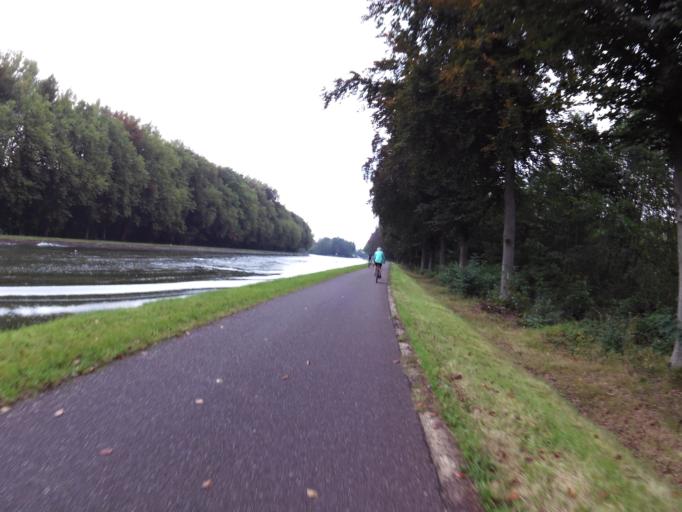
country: BE
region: Flanders
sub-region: Provincie Limburg
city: Kinrooi
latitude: 51.0743
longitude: 5.6982
